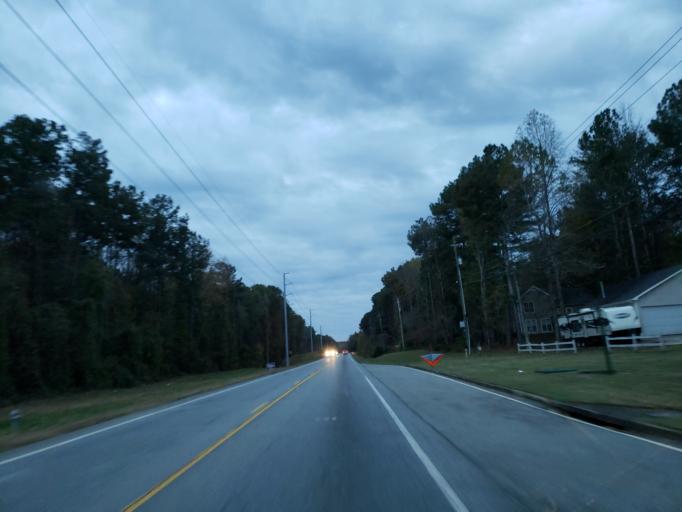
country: US
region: Georgia
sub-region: Paulding County
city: Hiram
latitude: 33.9645
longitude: -84.7396
